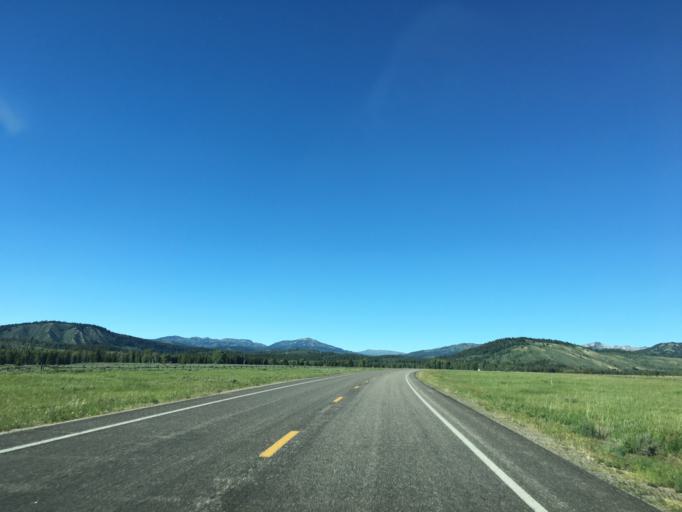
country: US
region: Wyoming
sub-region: Teton County
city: Jackson
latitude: 43.8191
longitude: -110.5239
